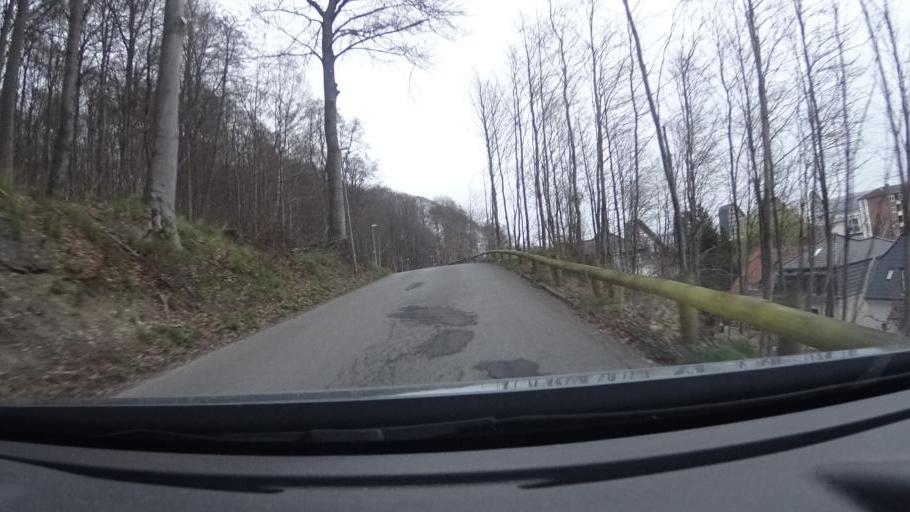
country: DK
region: South Denmark
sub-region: Vejle Kommune
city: Vejle
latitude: 55.7124
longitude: 9.5510
